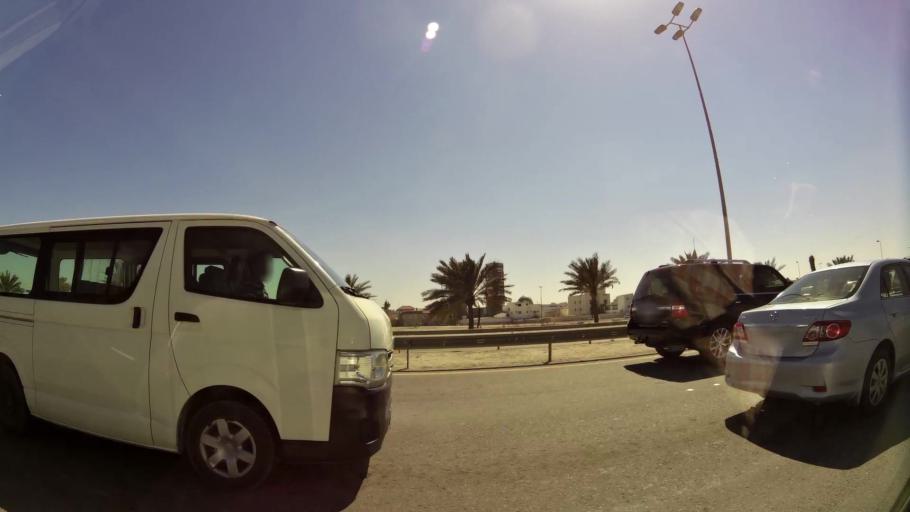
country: BH
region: Muharraq
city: Al Hadd
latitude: 26.2548
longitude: 50.6562
